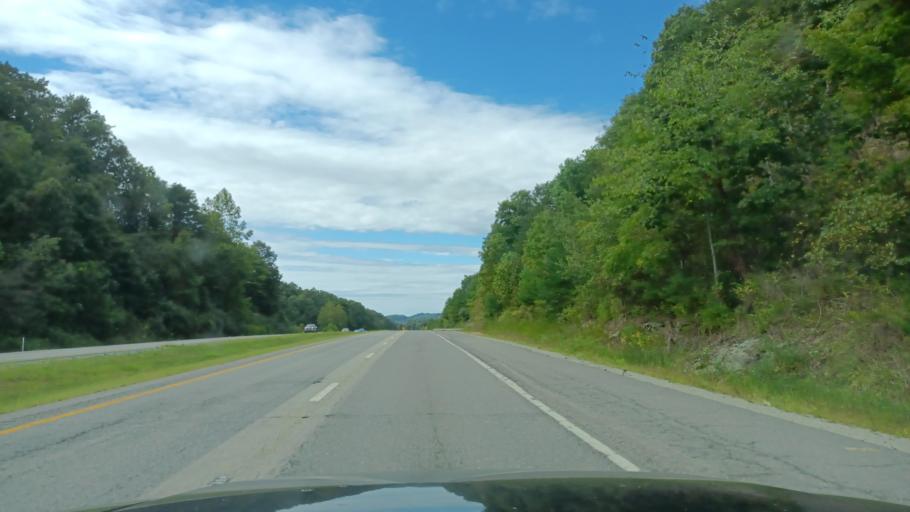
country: US
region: West Virginia
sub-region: Doddridge County
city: West Union
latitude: 39.2741
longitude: -80.8648
